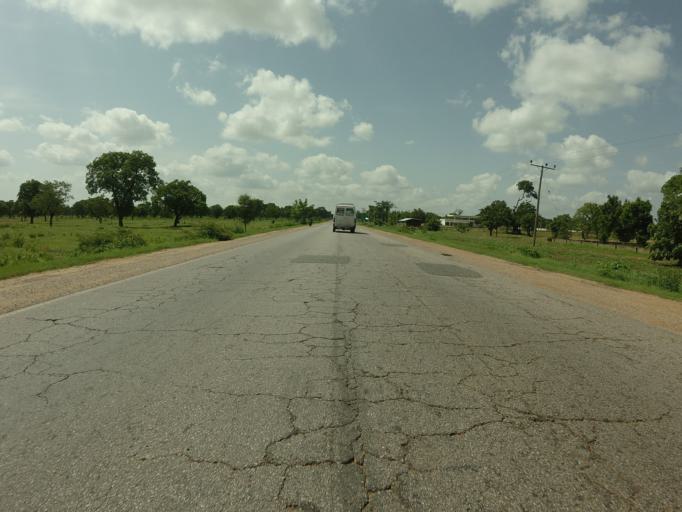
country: GH
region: Northern
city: Savelugu
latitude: 9.5698
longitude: -0.8351
